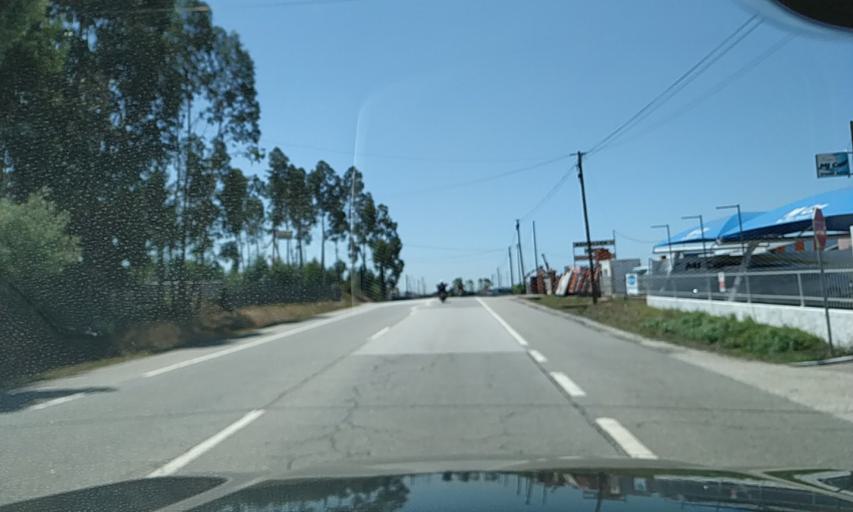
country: PT
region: Aveiro
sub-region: Anadia
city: Sangalhos
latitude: 40.4902
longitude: -8.4459
